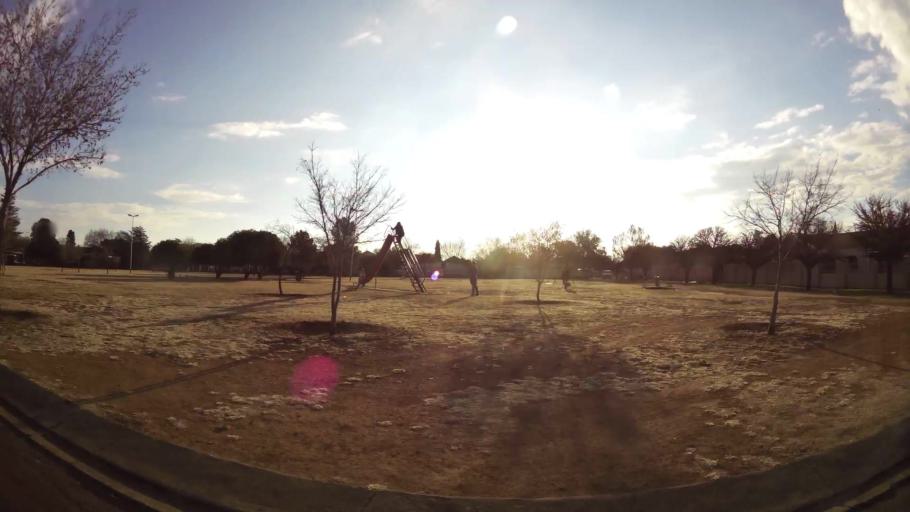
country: ZA
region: Orange Free State
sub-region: Mangaung Metropolitan Municipality
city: Bloemfontein
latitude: -29.1530
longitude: 26.1876
